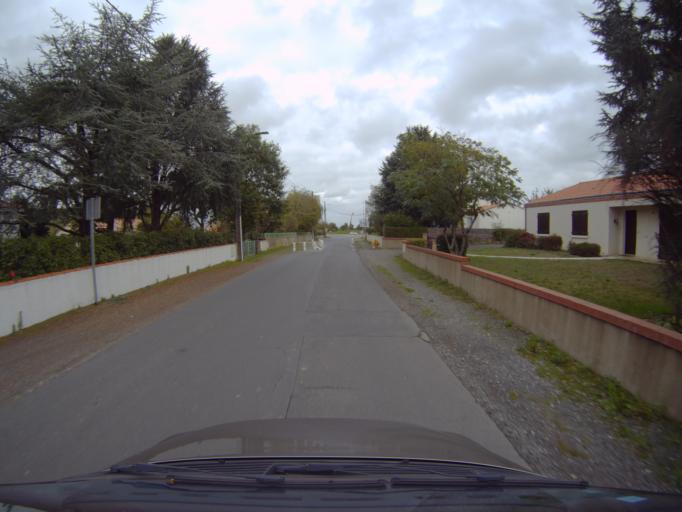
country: FR
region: Pays de la Loire
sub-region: Departement de la Loire-Atlantique
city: Clisson
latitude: 47.0959
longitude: -1.2731
